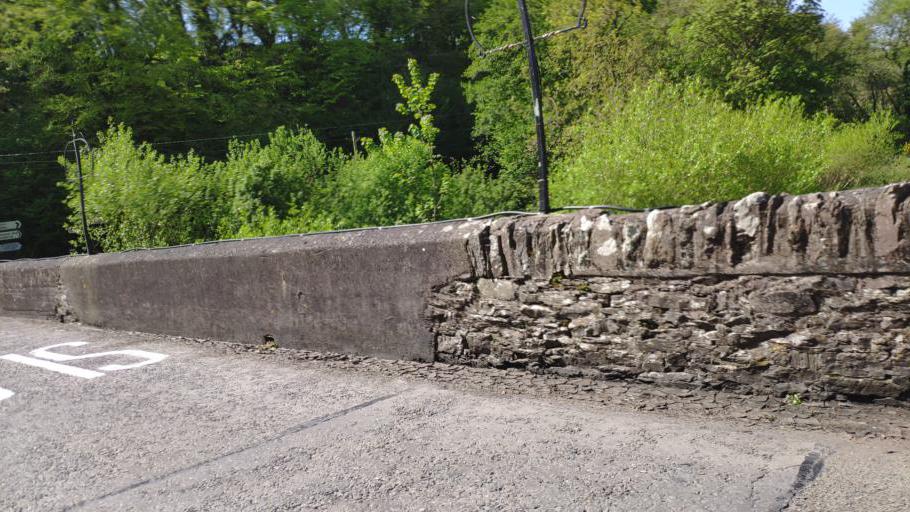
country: IE
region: Munster
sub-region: County Cork
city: Blarney
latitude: 51.9543
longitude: -8.5740
